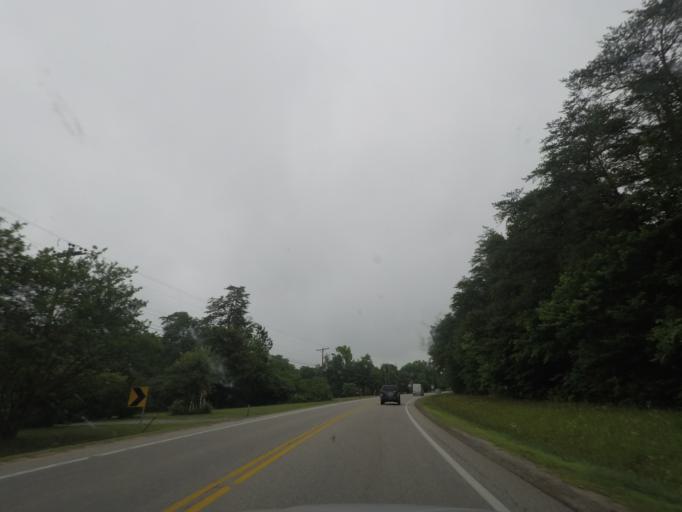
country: US
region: Virginia
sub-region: Prince Edward County
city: Hampden Sydney
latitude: 37.2482
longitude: -78.4424
